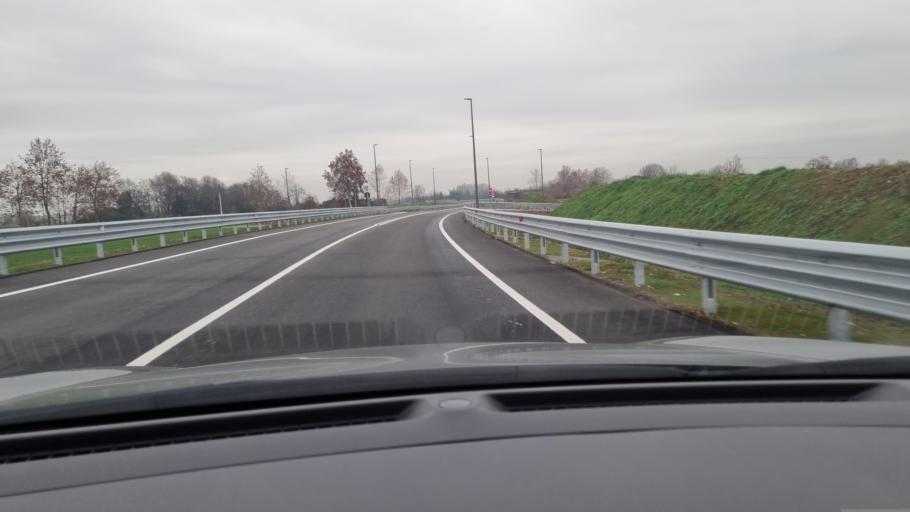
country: IT
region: Lombardy
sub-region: Provincia di Bergamo
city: Verdello
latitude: 45.6125
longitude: 9.6379
